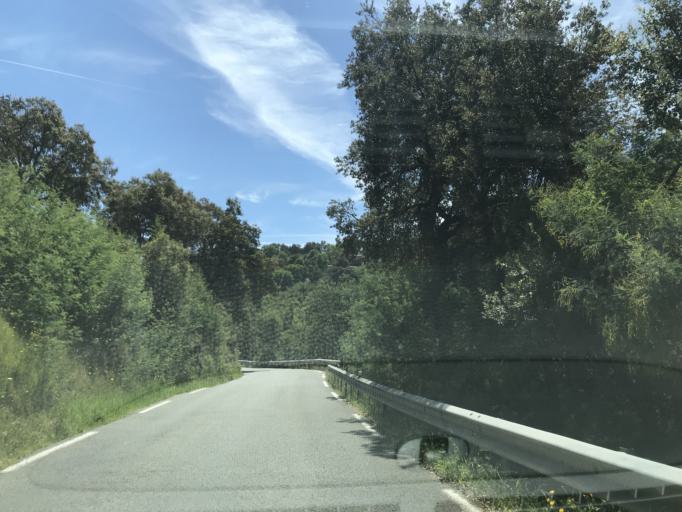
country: FR
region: Provence-Alpes-Cote d'Azur
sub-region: Departement des Alpes-Maritimes
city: Auribeau-sur-Siagne
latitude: 43.5865
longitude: 6.8971
